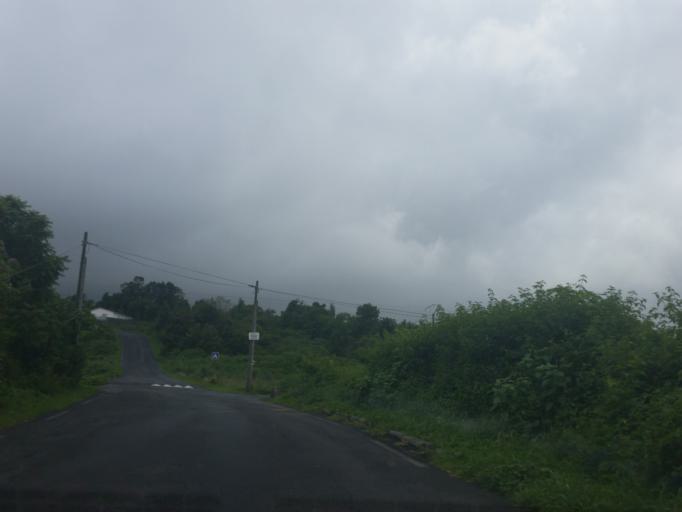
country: RE
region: Reunion
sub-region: Reunion
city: Le Tampon
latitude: -21.2416
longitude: 55.5152
